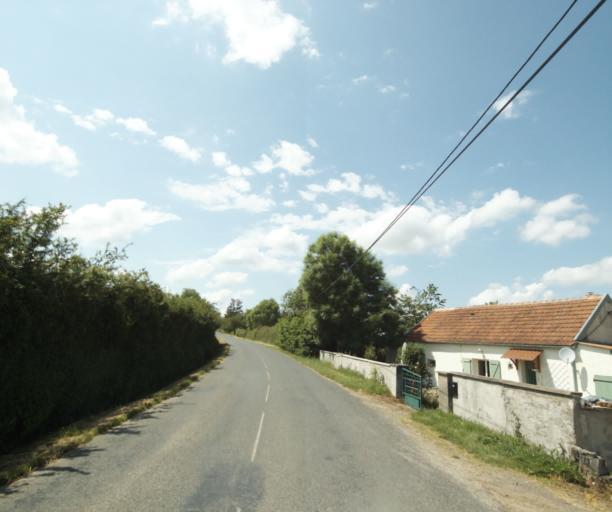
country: FR
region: Bourgogne
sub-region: Departement de Saone-et-Loire
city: Palinges
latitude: 46.5759
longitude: 4.1454
